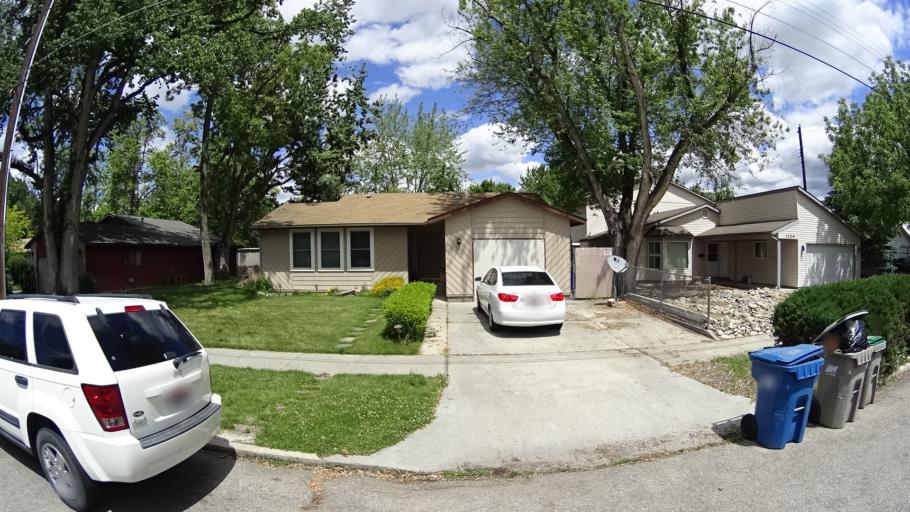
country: US
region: Idaho
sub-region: Ada County
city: Boise
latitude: 43.5837
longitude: -116.1975
